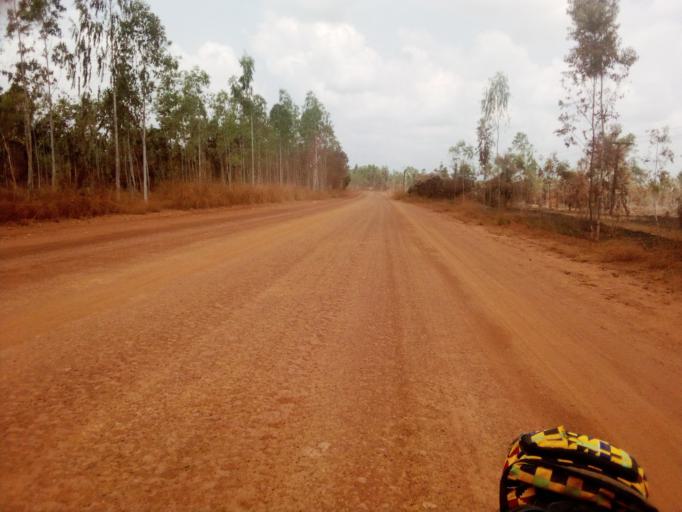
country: SL
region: Southern Province
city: Mogbwemo
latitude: 7.7552
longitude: -12.2939
